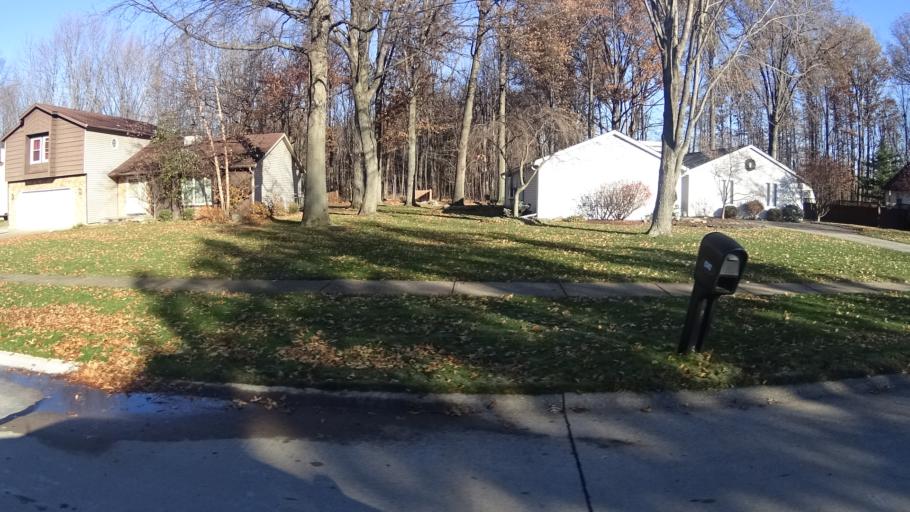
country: US
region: Ohio
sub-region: Lorain County
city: Sheffield Lake
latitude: 41.4604
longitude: -82.0737
